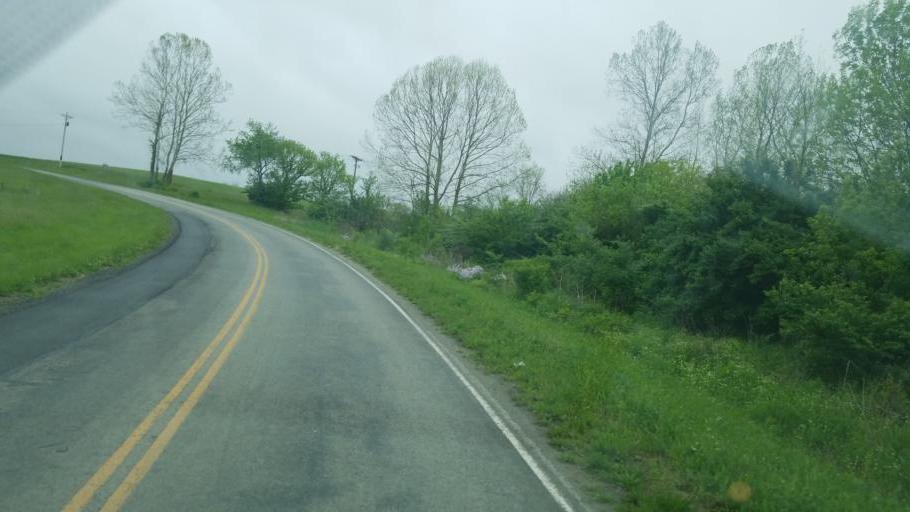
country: US
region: Ohio
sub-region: Highland County
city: Greenfield
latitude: 39.3334
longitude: -83.4620
